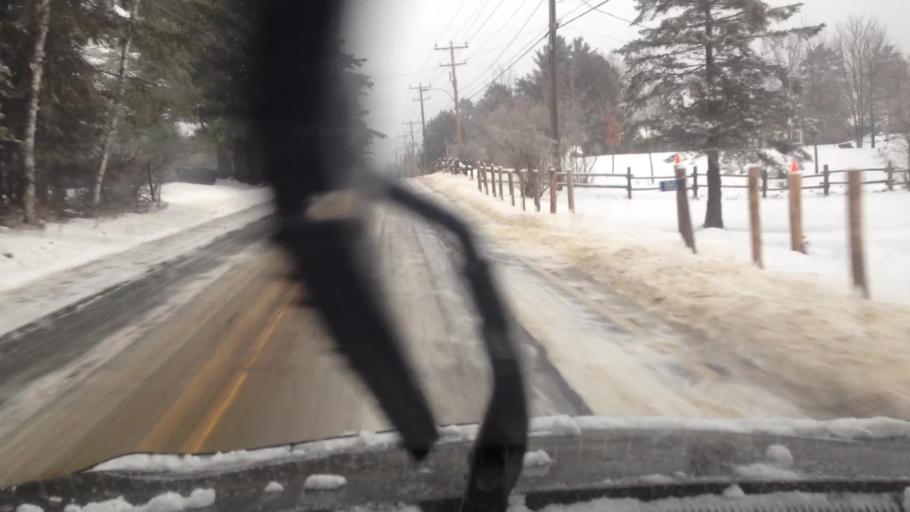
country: CA
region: Quebec
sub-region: Laurentides
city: Mont-Tremblant
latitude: 45.9775
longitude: -74.6137
